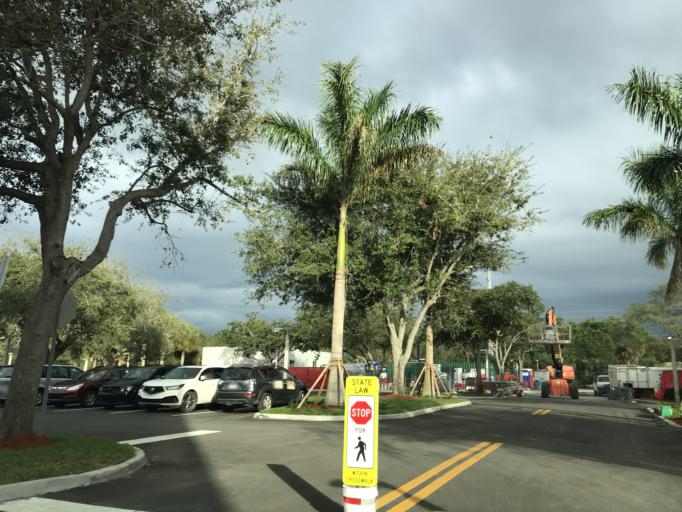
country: US
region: Florida
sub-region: Palm Beach County
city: Jupiter
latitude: 26.9228
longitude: -80.0955
